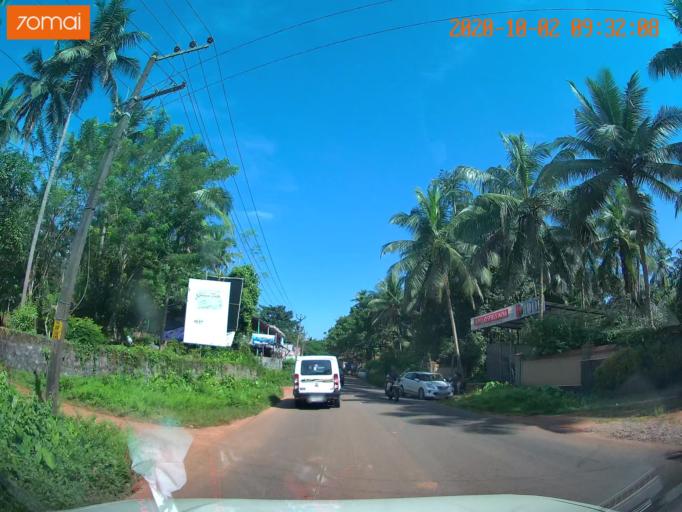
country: IN
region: Kerala
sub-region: Kozhikode
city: Nadapuram
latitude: 11.6263
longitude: 75.7572
